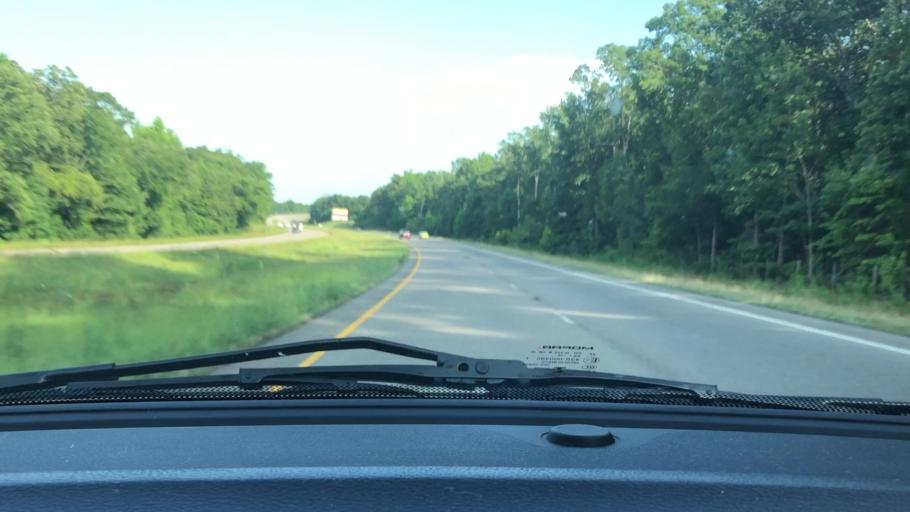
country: US
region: North Carolina
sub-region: Chatham County
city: Farmville
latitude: 35.5732
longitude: -79.3081
